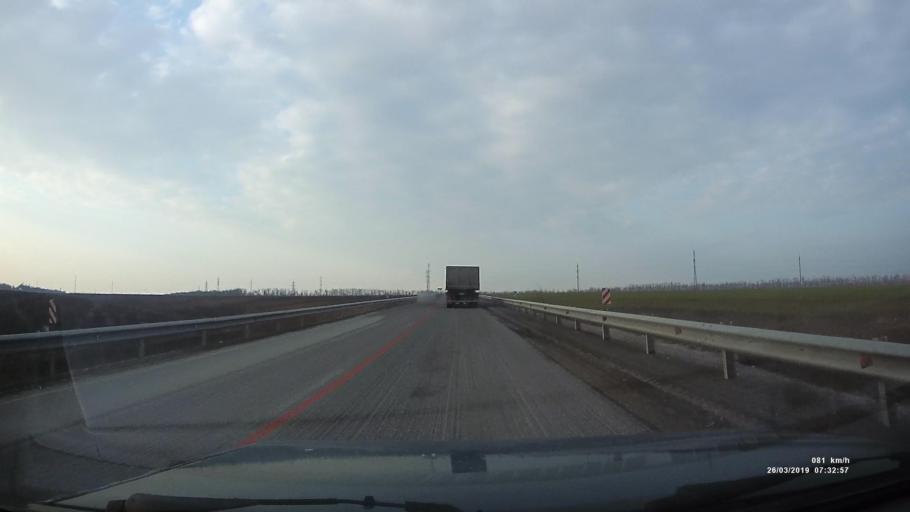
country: RU
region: Rostov
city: Novobessergenovka
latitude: 47.2194
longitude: 38.7733
